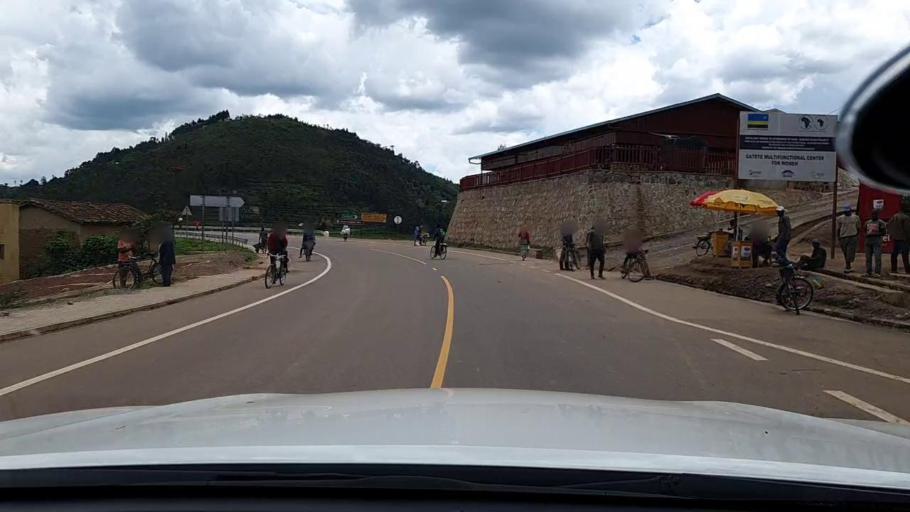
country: RW
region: Northern Province
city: Byumba
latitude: -1.6549
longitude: 29.9072
